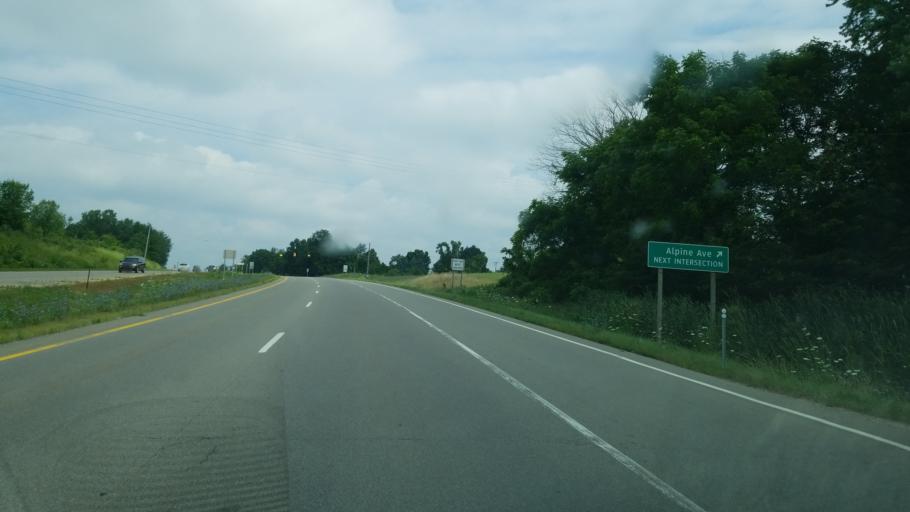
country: US
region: Michigan
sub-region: Kent County
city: Comstock Park
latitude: 43.0909
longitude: -85.6902
